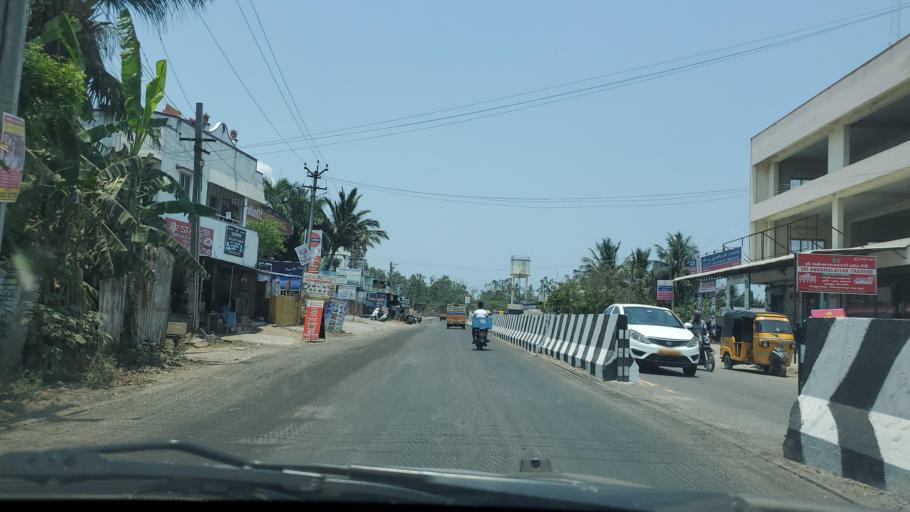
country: IN
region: Tamil Nadu
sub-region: Kancheepuram
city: Vengavasal
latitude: 12.8656
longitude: 80.1757
